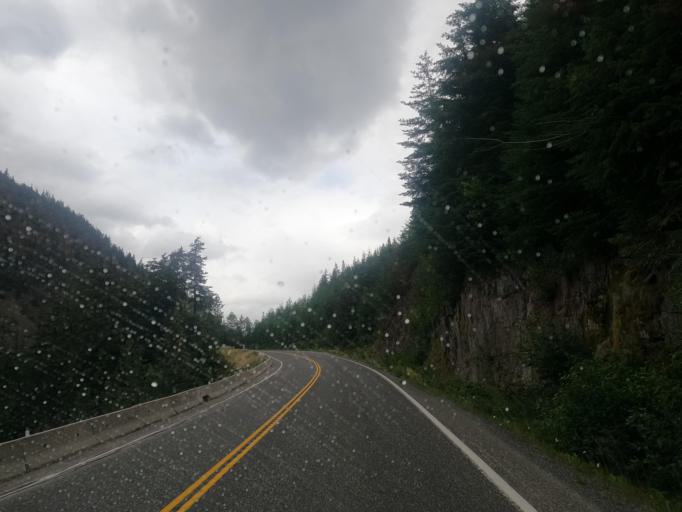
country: CA
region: British Columbia
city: Lillooet
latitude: 50.4917
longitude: -122.1966
